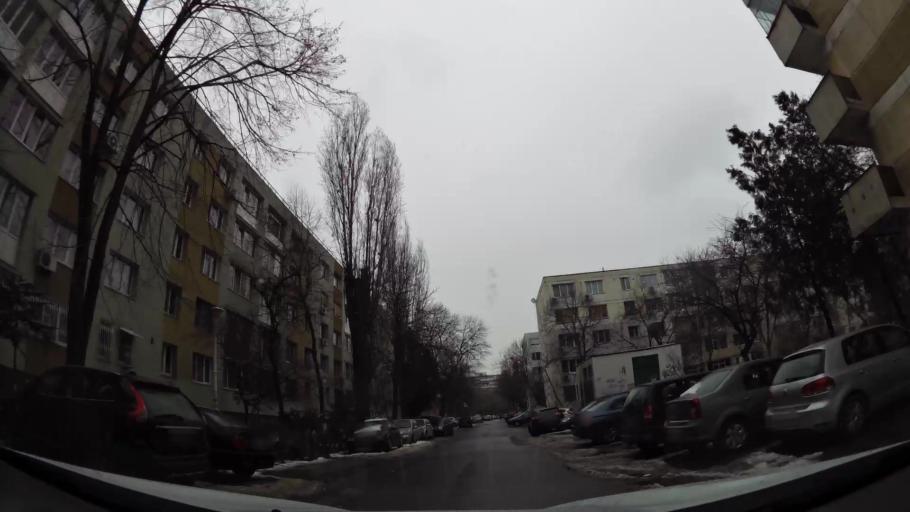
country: RO
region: Ilfov
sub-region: Comuna Chiajna
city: Rosu
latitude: 44.4229
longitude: 26.0214
